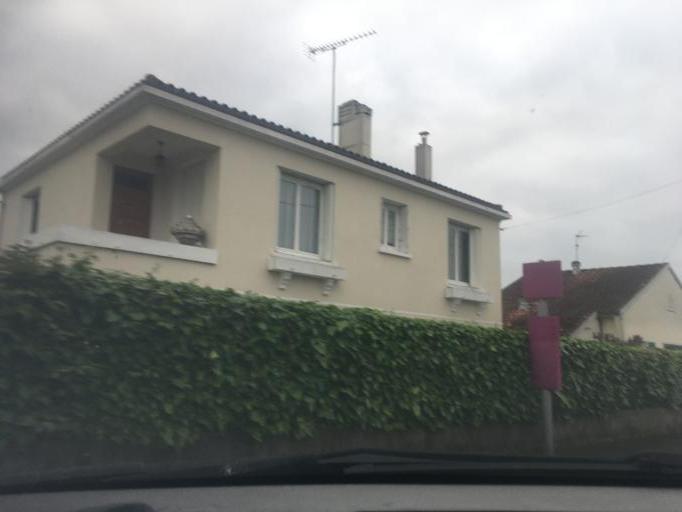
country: FR
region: Poitou-Charentes
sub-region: Departement de la Charente
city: Cognac
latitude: 45.6836
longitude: -0.3356
